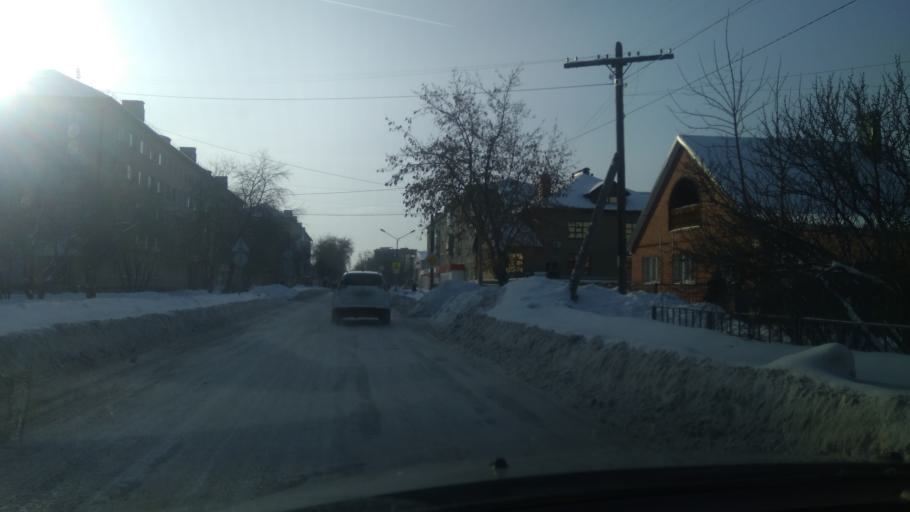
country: RU
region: Sverdlovsk
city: Sukhoy Log
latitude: 56.9048
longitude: 62.0323
